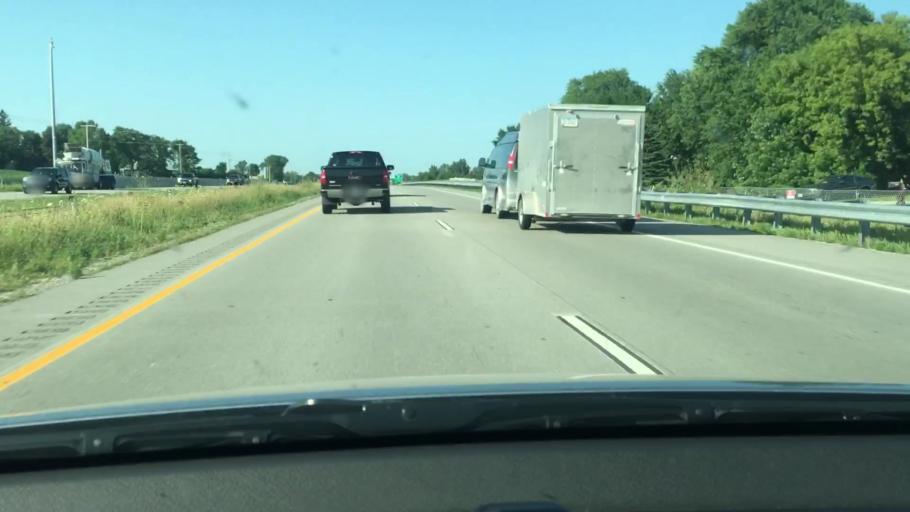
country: US
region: Wisconsin
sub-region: Brown County
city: Wrightstown
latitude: 44.3689
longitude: -88.1760
